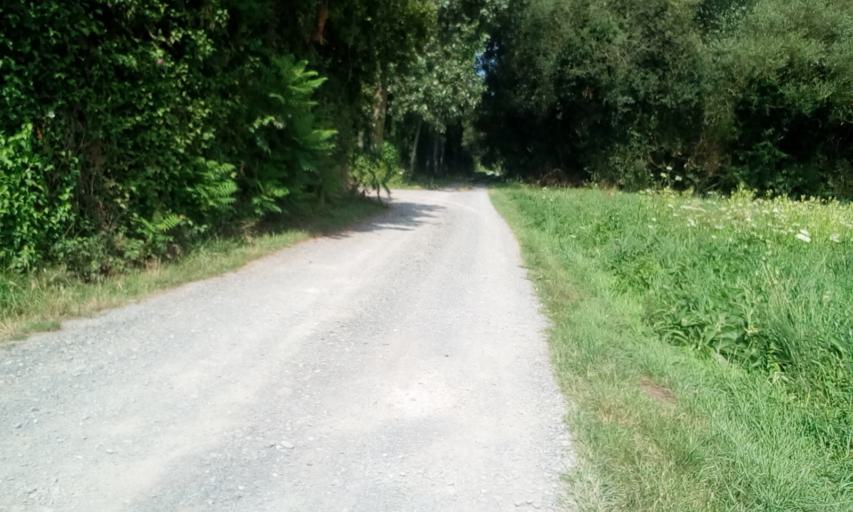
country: FR
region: Lower Normandy
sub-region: Departement du Calvados
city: Argences
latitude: 49.1378
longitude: -0.1714
